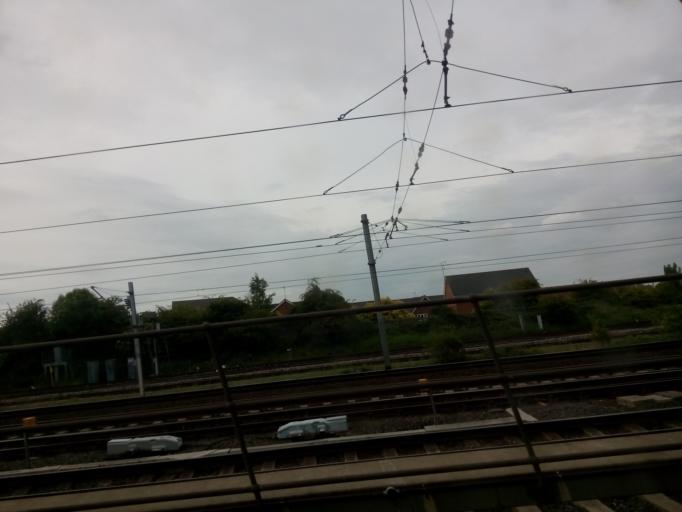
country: GB
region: England
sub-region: South Tyneside
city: Hebburn
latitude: 54.9527
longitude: -1.5397
